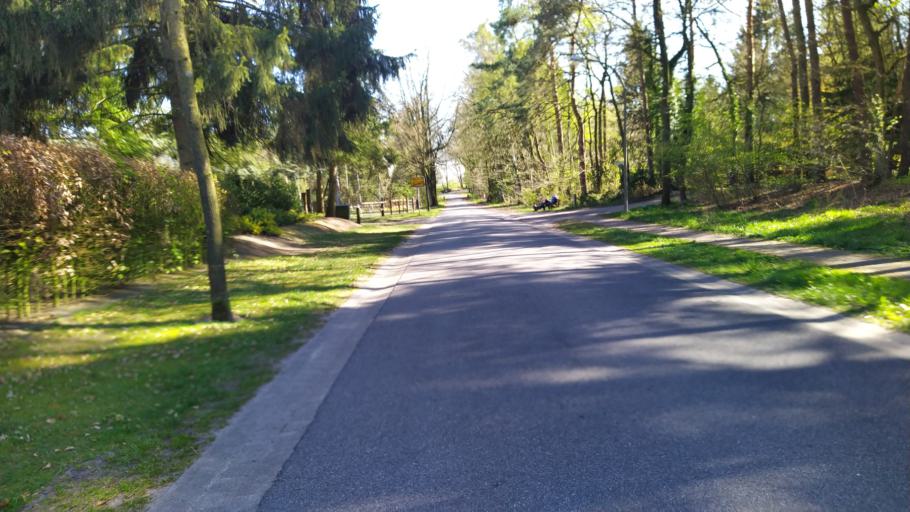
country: DE
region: Lower Saxony
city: Heeslingen
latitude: 53.3317
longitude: 9.3813
